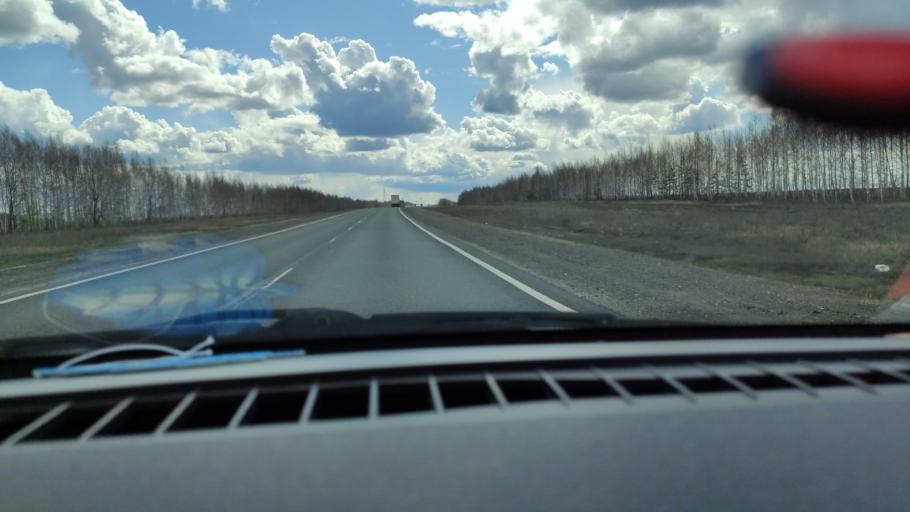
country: RU
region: Saratov
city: Dukhovnitskoye
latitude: 52.8443
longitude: 48.2508
